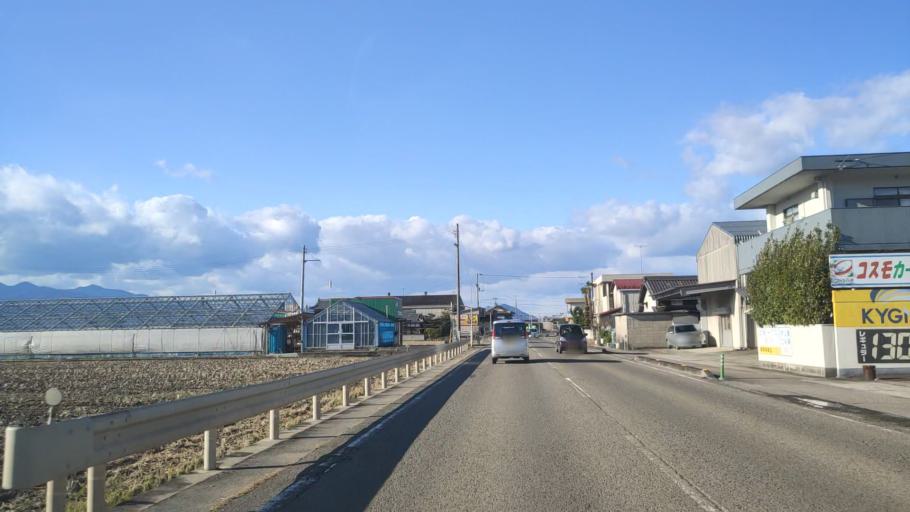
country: JP
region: Ehime
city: Saijo
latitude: 33.9147
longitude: 133.1065
